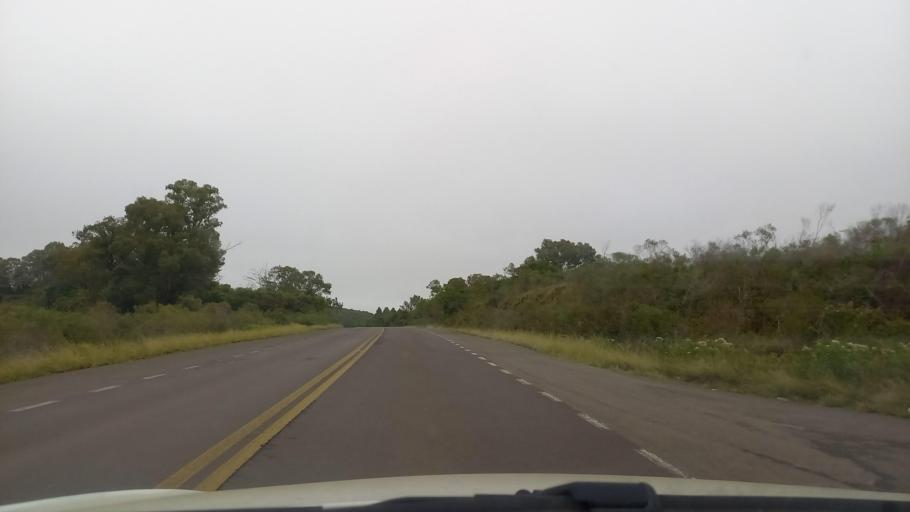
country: BR
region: Rio Grande do Sul
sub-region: Cacequi
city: Cacequi
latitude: -30.0373
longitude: -54.5880
